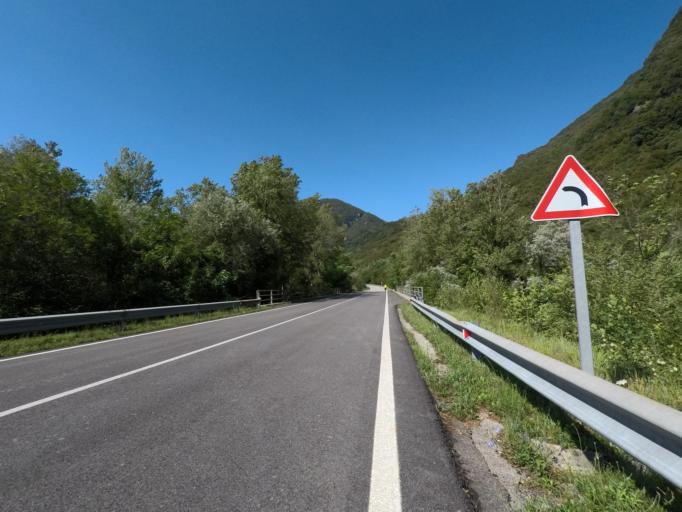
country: IT
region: Friuli Venezia Giulia
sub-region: Provincia di Udine
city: Trasaghis
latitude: 46.2676
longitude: 13.0500
